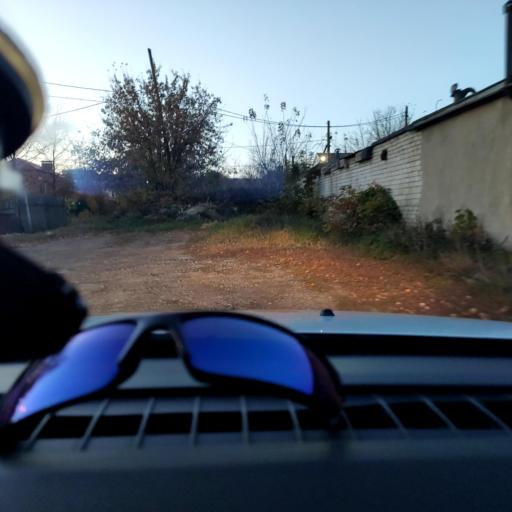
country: RU
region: Samara
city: Samara
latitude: 53.2271
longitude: 50.2231
